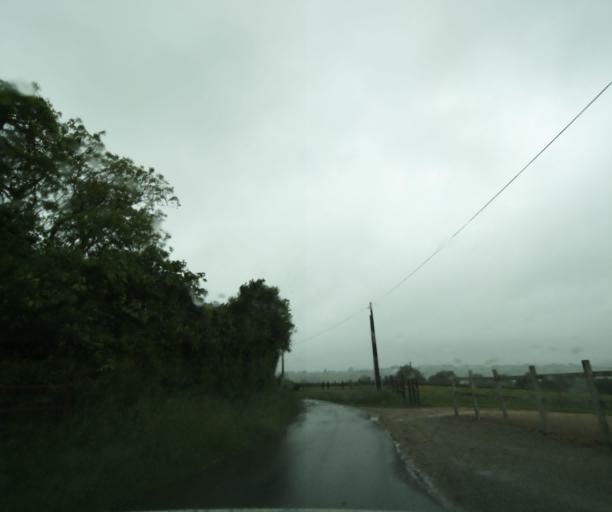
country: FR
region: Bourgogne
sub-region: Departement de Saone-et-Loire
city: Ciry-le-Noble
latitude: 46.5372
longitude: 4.3592
